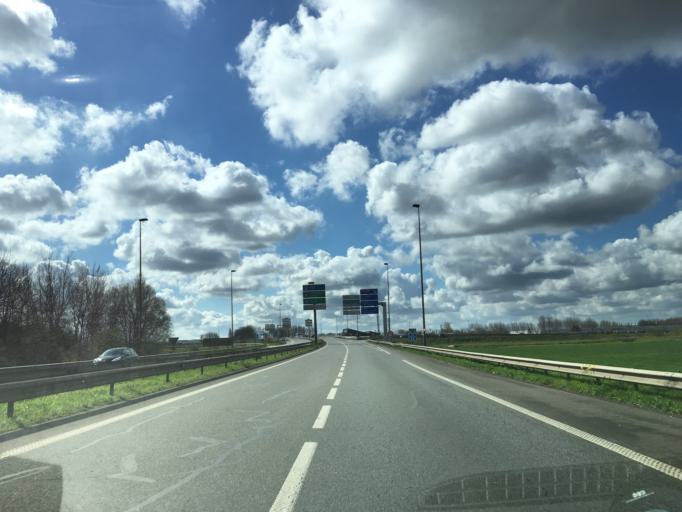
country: FR
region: Nord-Pas-de-Calais
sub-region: Departement du Nord
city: Fort-Mardyck
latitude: 51.0110
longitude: 2.3241
